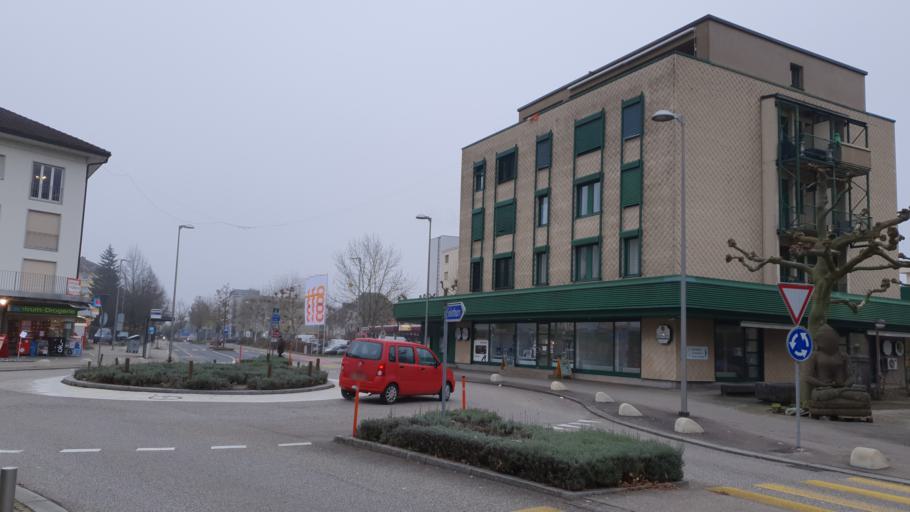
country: CH
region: Solothurn
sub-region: Bezirk Wasseramt
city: Zuchwil
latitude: 47.2036
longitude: 7.5573
